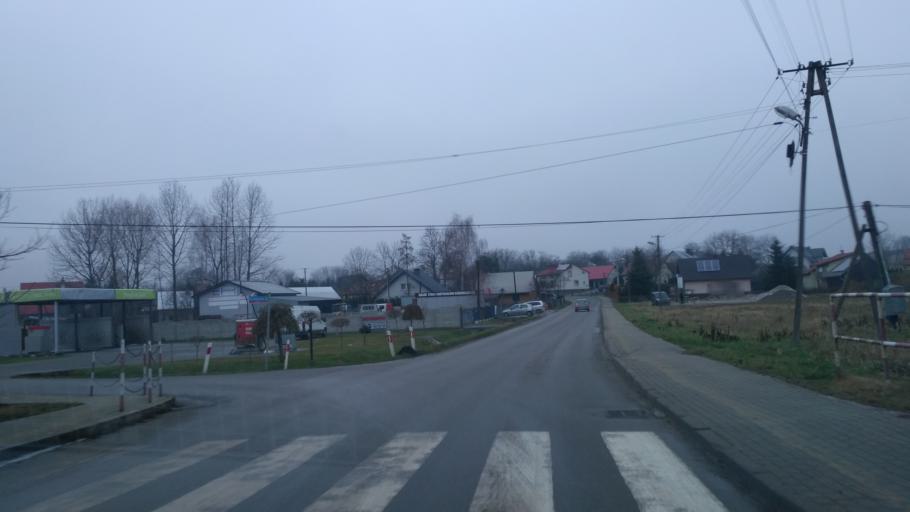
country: PL
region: Subcarpathian Voivodeship
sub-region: Powiat przeworski
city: Zarzecze
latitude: 49.9877
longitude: 22.5328
